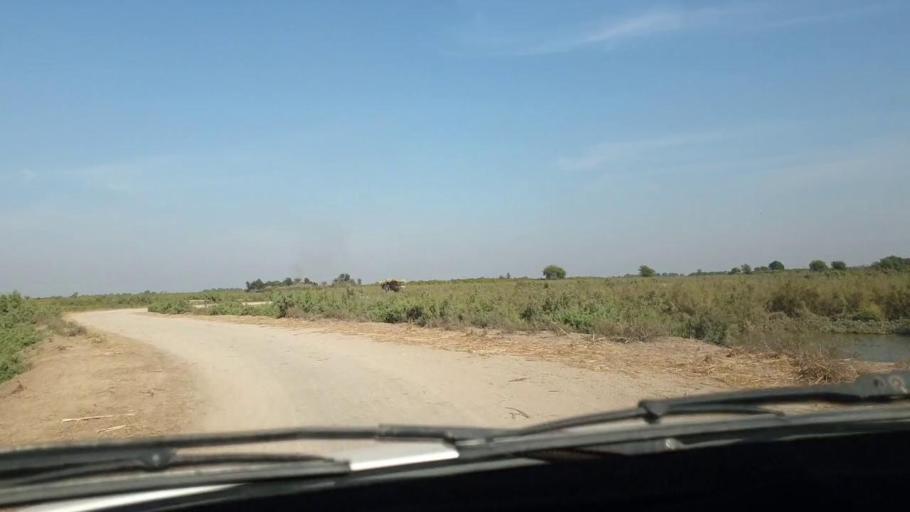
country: PK
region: Sindh
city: Bulri
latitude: 24.9503
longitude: 68.4257
